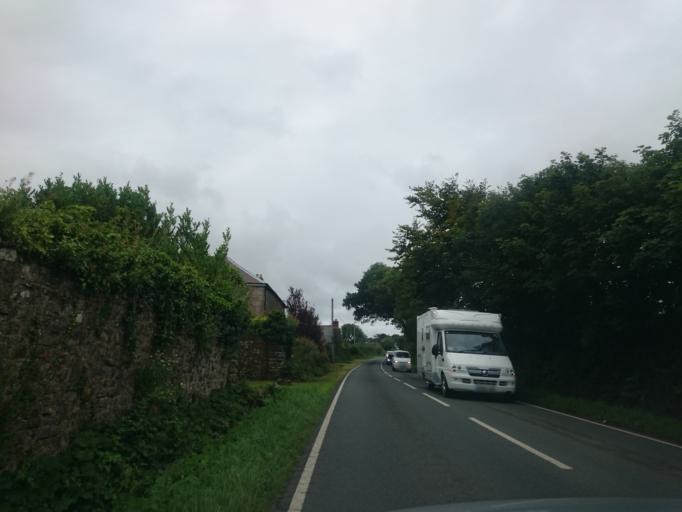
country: GB
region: Wales
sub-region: Pembrokeshire
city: Haverfordwest
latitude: 51.7834
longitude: -4.9730
